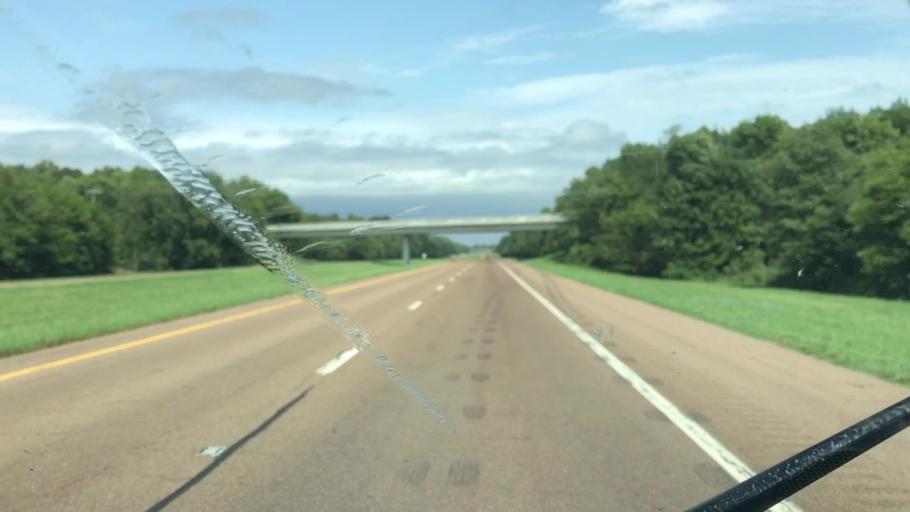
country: US
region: Tennessee
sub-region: Obion County
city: South Fulton
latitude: 36.4815
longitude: -88.9425
